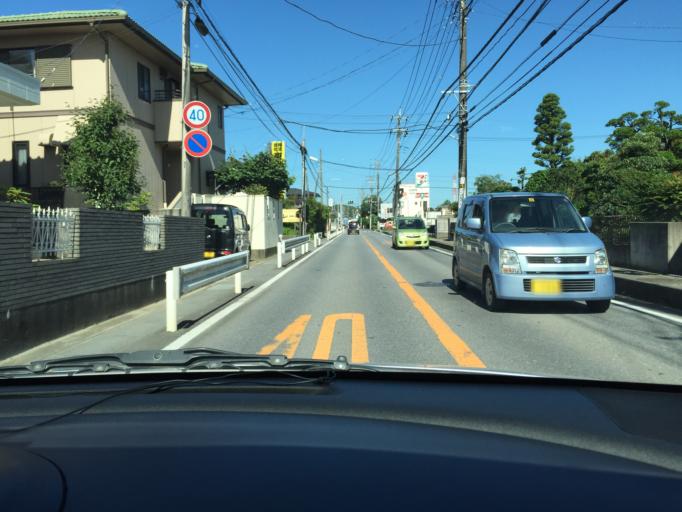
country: JP
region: Ibaraki
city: Naka
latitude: 36.0767
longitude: 140.1856
